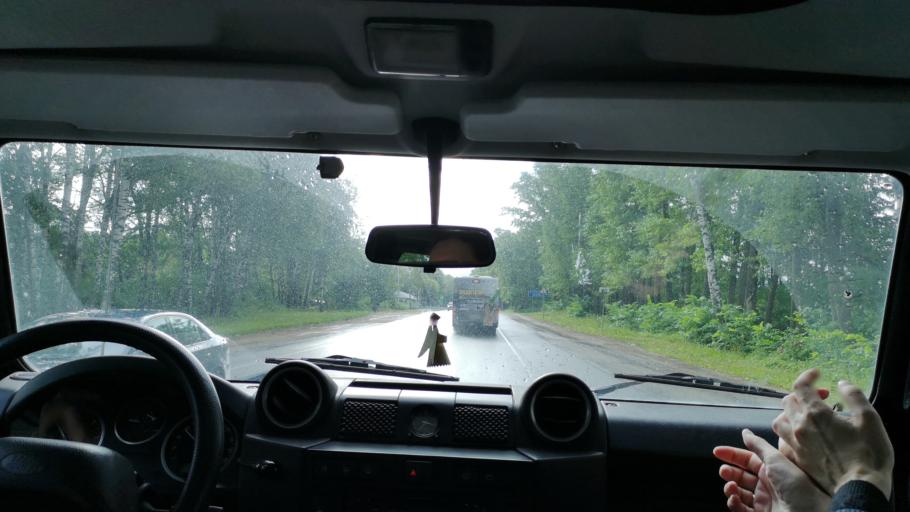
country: RU
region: Moskovskaya
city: Gorshkovo
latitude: 56.3681
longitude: 37.4529
